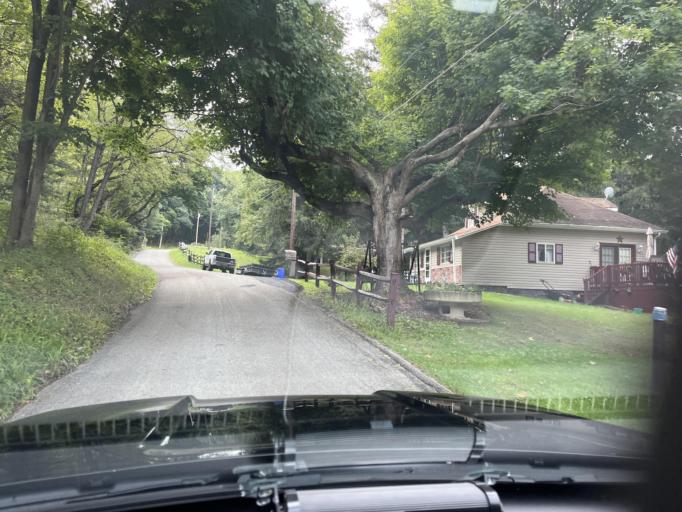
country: US
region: Pennsylvania
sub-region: Fayette County
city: Hopwood
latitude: 39.8652
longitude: -79.6957
